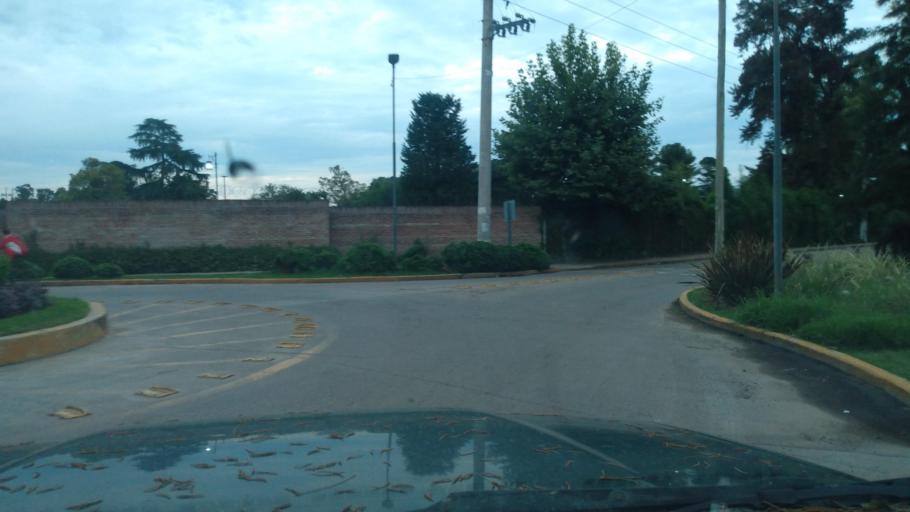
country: AR
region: Buenos Aires
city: Hurlingham
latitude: -34.5725
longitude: -58.7071
